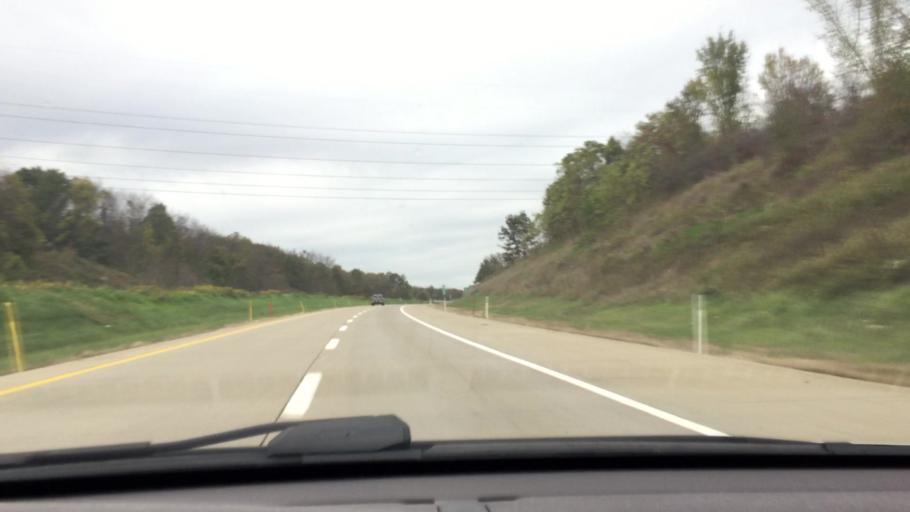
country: US
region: Pennsylvania
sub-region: Beaver County
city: Big Beaver
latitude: 40.8211
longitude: -80.3713
